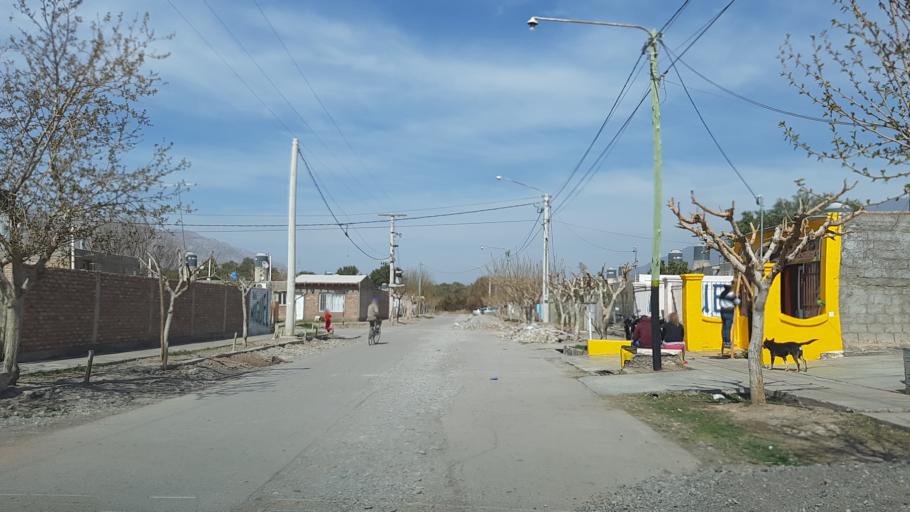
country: AR
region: San Juan
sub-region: Departamento de Zonda
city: Zonda
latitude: -31.5528
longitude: -68.7320
